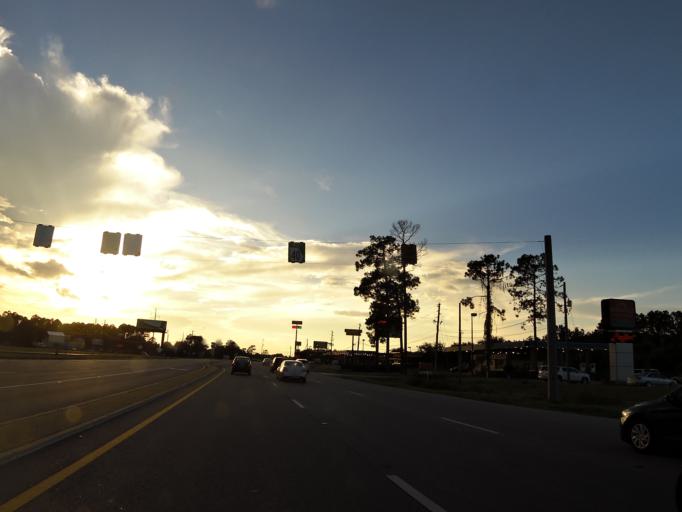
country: US
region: Georgia
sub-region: Camden County
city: Kingsland
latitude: 30.7917
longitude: -81.6621
